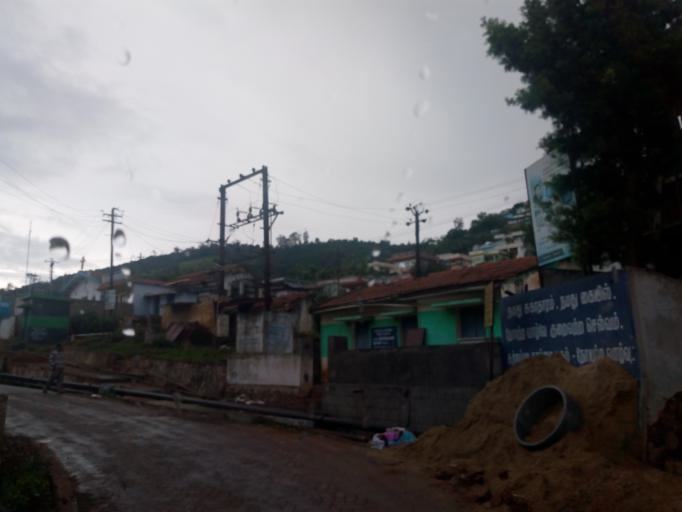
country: IN
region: Tamil Nadu
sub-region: Nilgiri
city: Wellington
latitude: 11.3607
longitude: 76.8348
